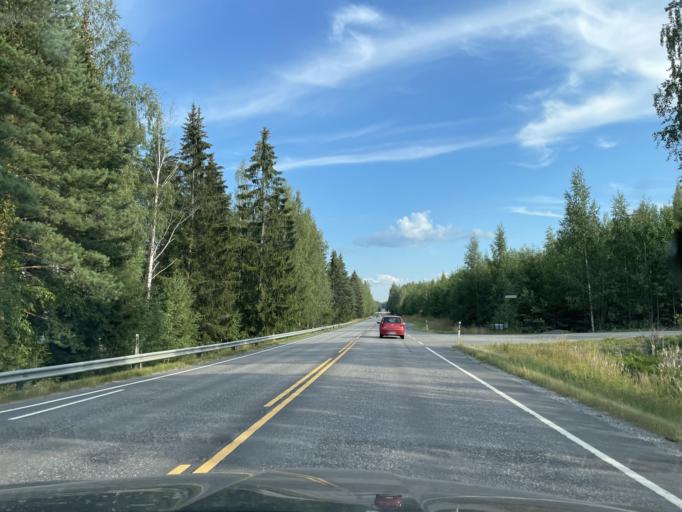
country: FI
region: Paijanne Tavastia
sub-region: Lahti
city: Padasjoki
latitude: 61.3637
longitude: 25.2195
